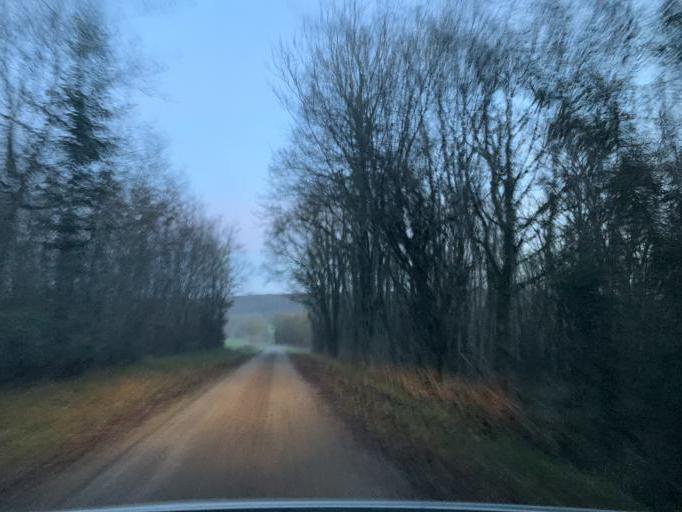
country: FR
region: Bourgogne
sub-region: Departement de l'Yonne
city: Fontenailles
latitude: 47.5564
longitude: 3.3618
